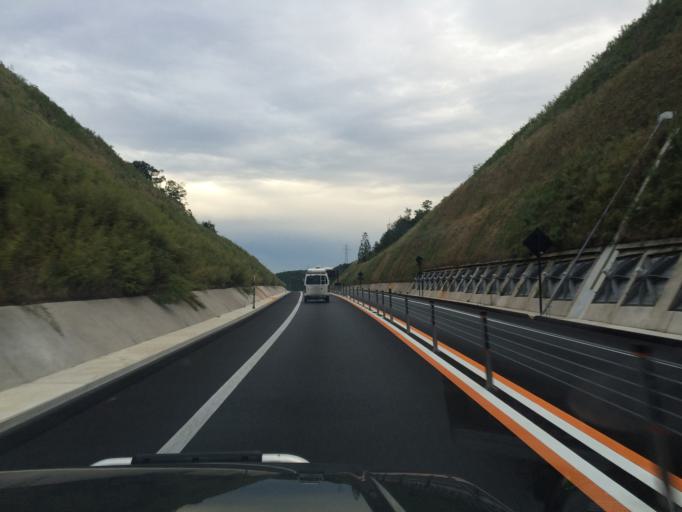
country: JP
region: Tottori
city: Tottori
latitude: 35.4925
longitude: 134.1420
